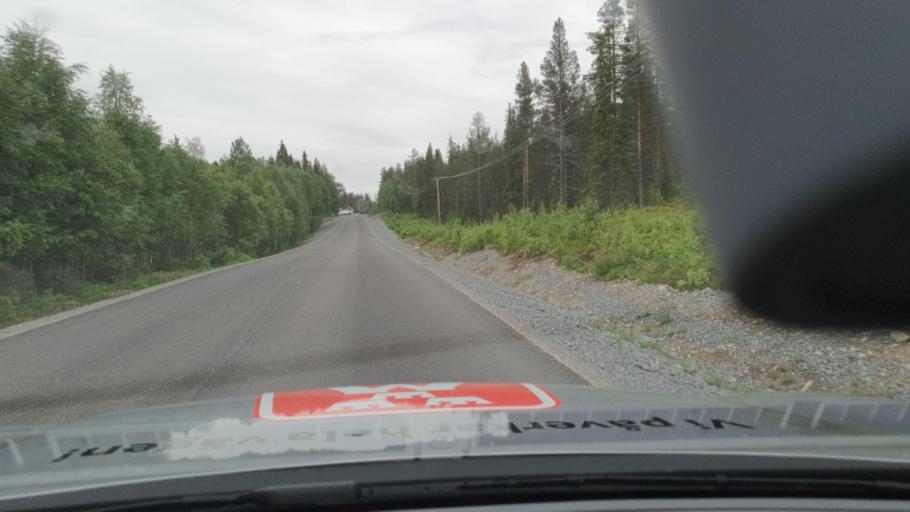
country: SE
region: Norrbotten
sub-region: Overtornea Kommun
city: OEvertornea
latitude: 66.6216
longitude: 23.2861
